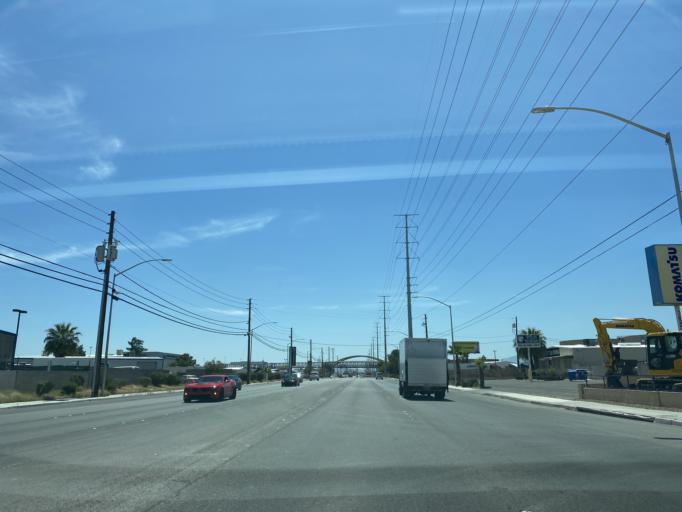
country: US
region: Nevada
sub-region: Clark County
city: North Las Vegas
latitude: 36.2300
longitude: -115.1183
